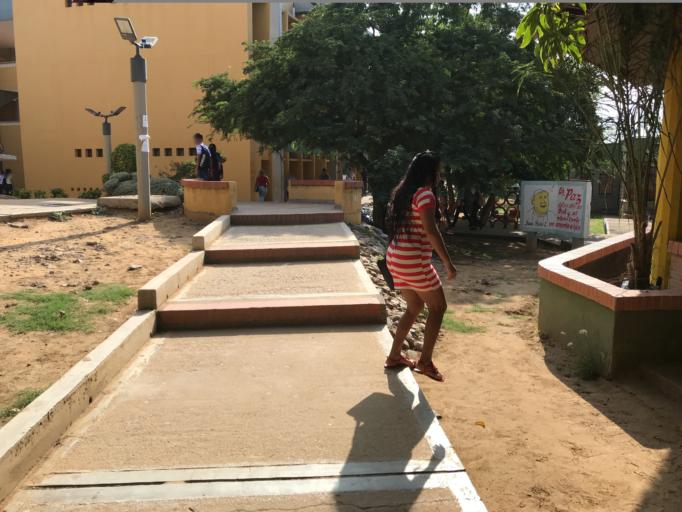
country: CO
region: La Guajira
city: Riohacha
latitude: 11.5128
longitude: -72.8702
